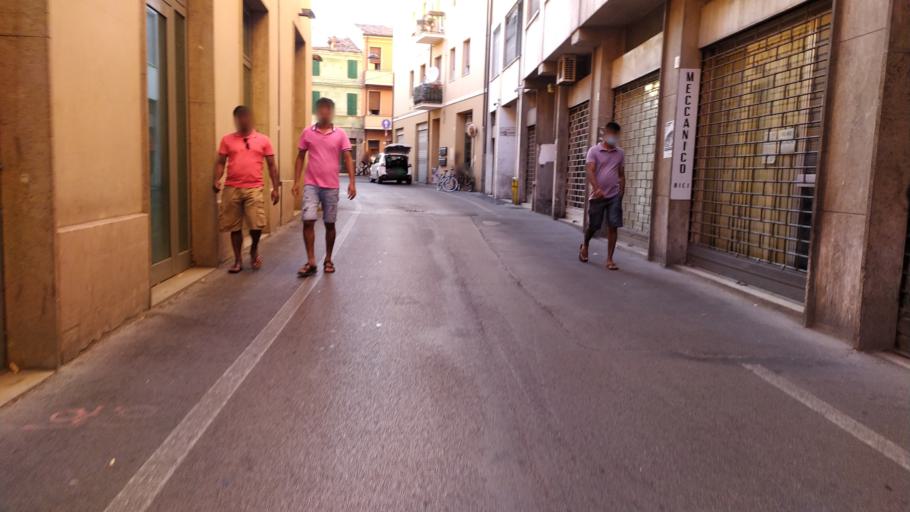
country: IT
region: Emilia-Romagna
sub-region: Forli-Cesena
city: Forli
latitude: 44.2245
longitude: 12.0432
